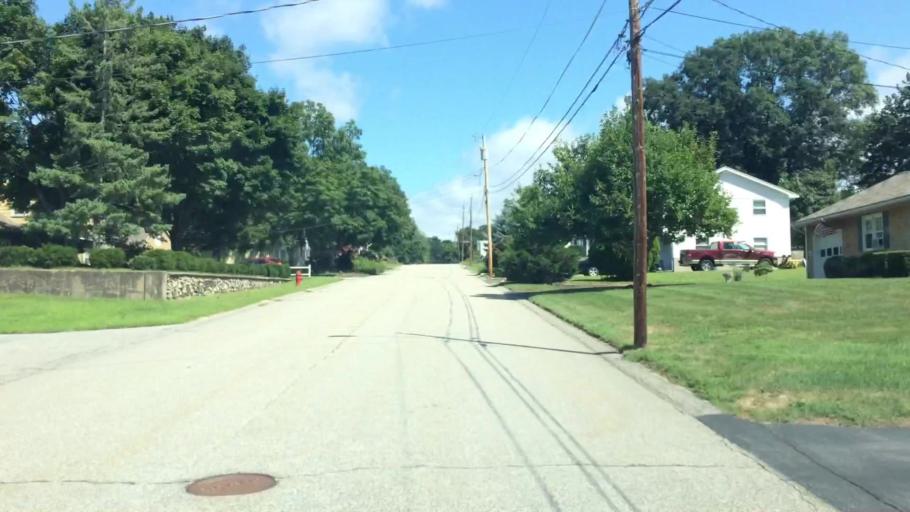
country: US
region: Rhode Island
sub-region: Providence County
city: Cumberland Hill
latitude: 41.9864
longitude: -71.4870
